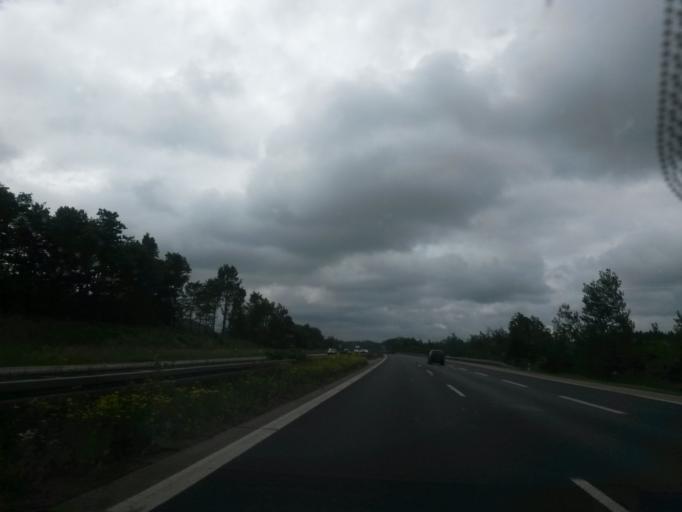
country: DE
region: Bavaria
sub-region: Regierungsbezirk Unterfranken
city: Schondra
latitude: 50.2935
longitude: 9.8504
